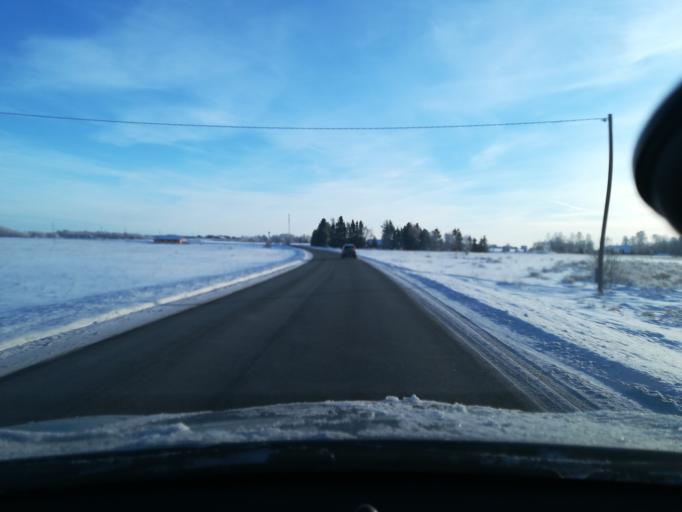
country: EE
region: Harju
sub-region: Harku vald
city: Tabasalu
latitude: 59.3700
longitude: 24.4763
